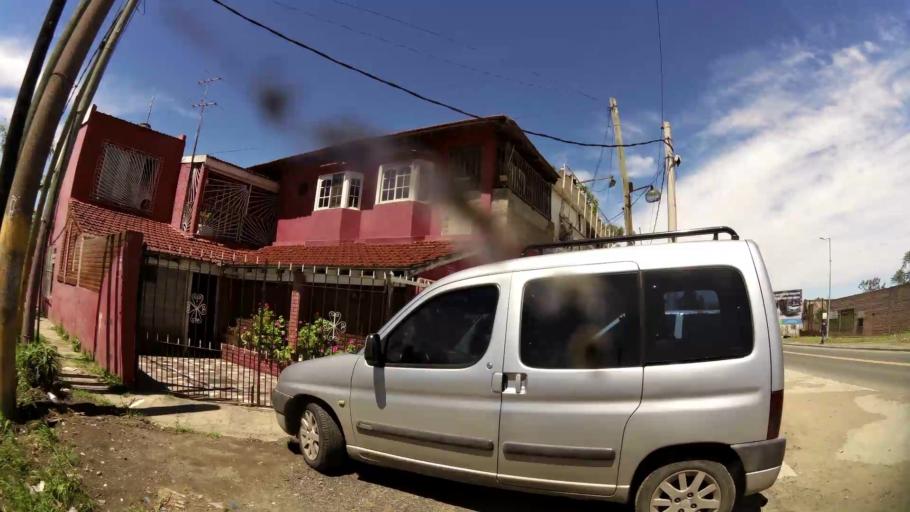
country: AR
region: Buenos Aires
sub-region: Partido de Quilmes
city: Quilmes
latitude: -34.7402
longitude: -58.3180
